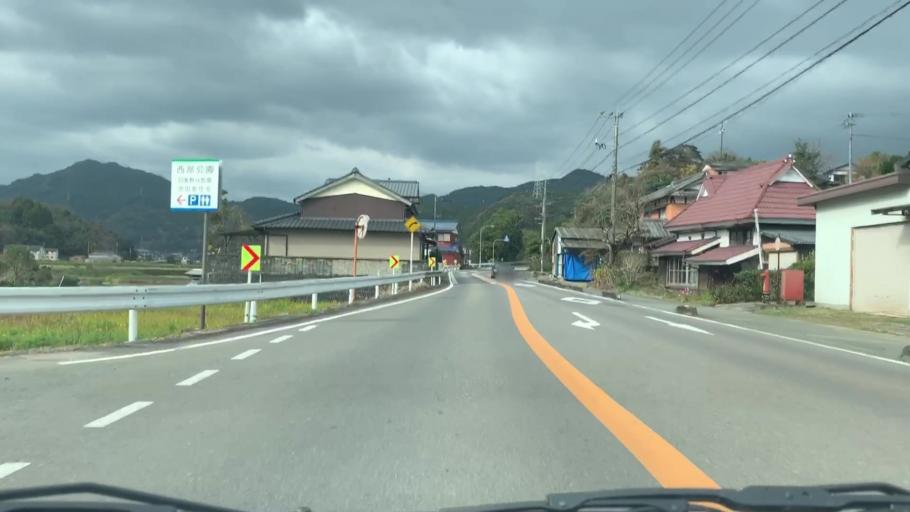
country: JP
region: Saga Prefecture
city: Ureshinomachi-shimojuku
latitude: 33.1308
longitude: 130.0319
